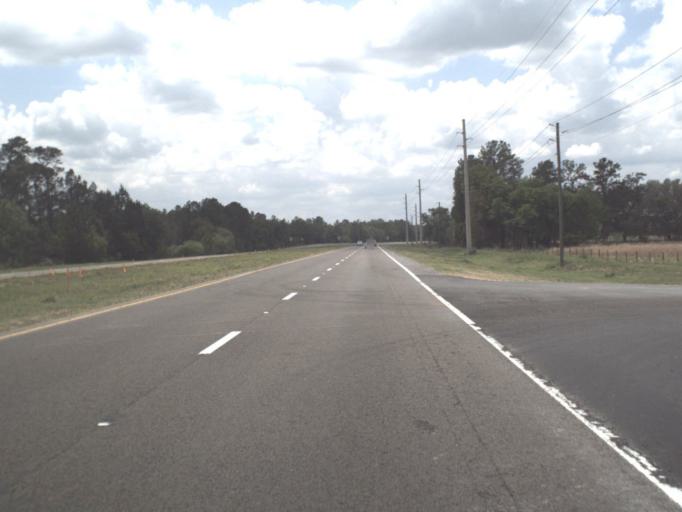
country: US
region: Florida
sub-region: Sumter County
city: Wildwood
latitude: 28.8660
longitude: -82.1508
